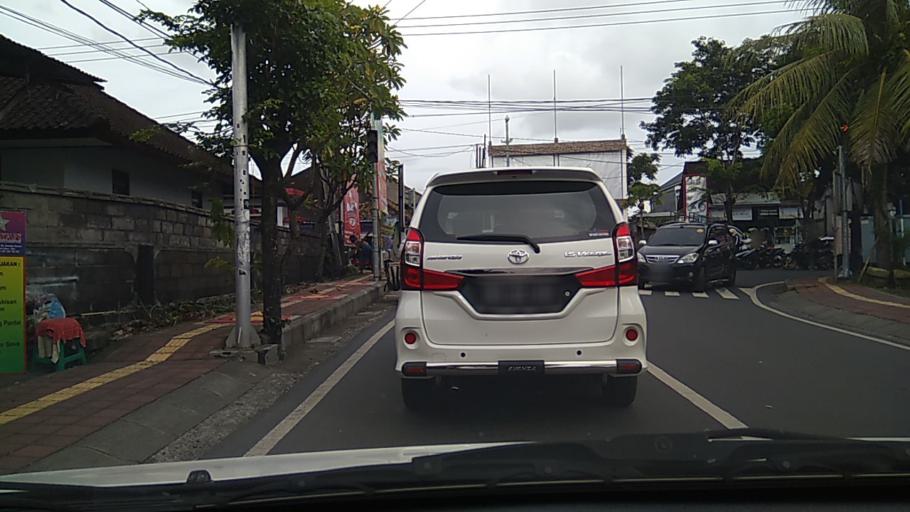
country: ID
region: Bali
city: Banjar Gunungpande
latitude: -8.6417
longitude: 115.1552
